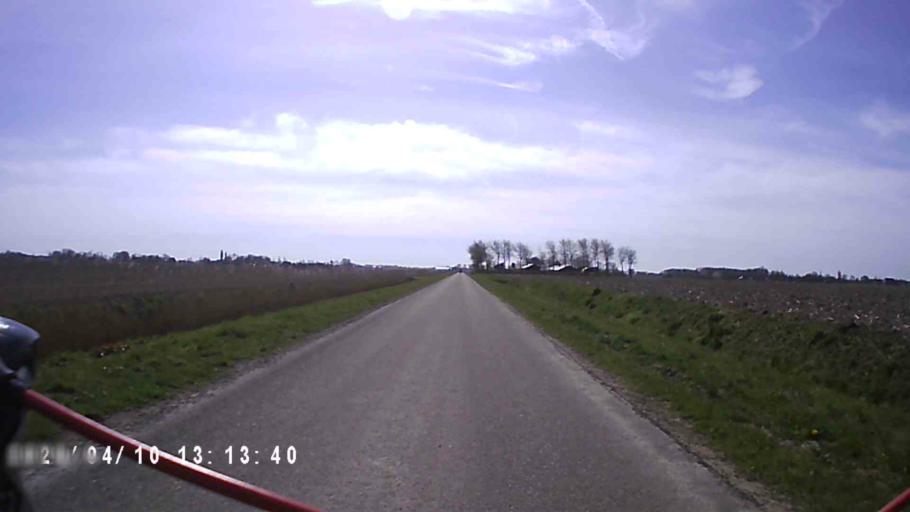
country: NL
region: Groningen
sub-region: Gemeente De Marne
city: Ulrum
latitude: 53.4030
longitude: 6.4178
